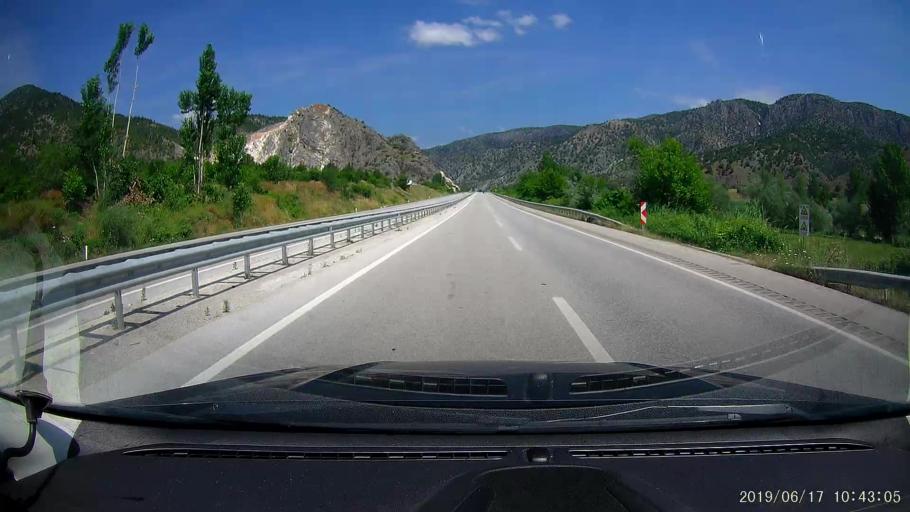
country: TR
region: Corum
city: Kargi
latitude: 41.0582
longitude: 34.5418
